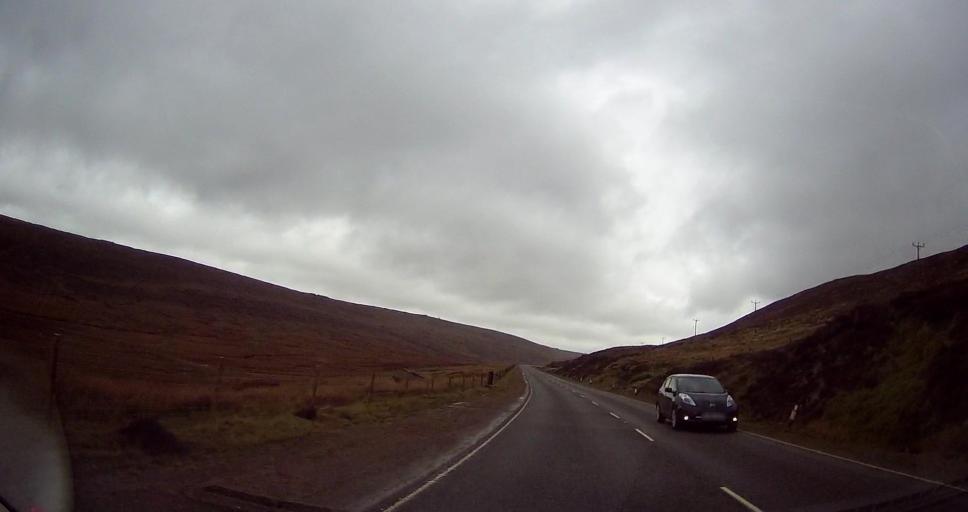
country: GB
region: Scotland
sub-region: Shetland Islands
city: Lerwick
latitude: 60.3048
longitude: -1.2395
